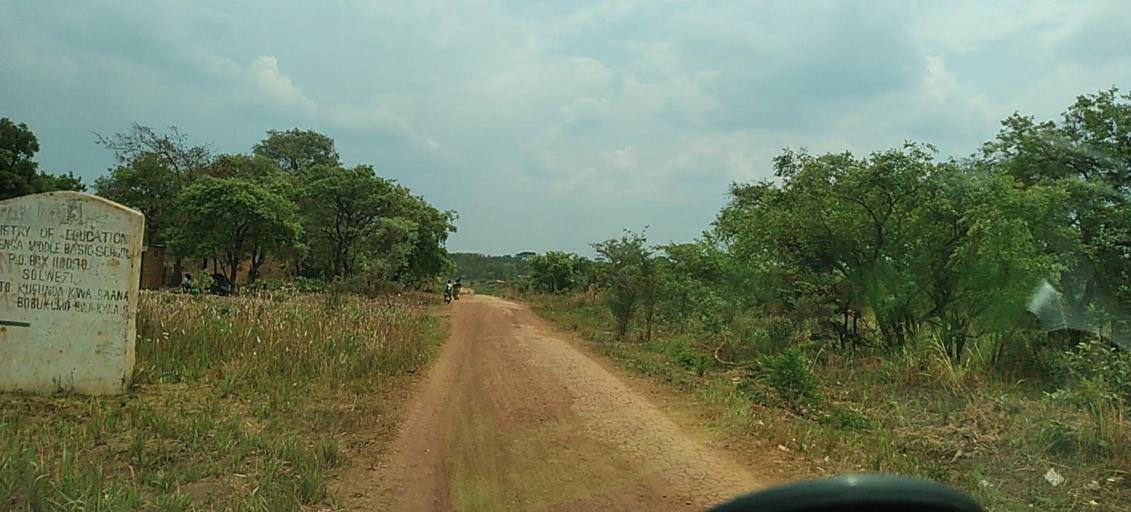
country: ZM
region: North-Western
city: Kansanshi
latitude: -11.9924
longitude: 26.2829
